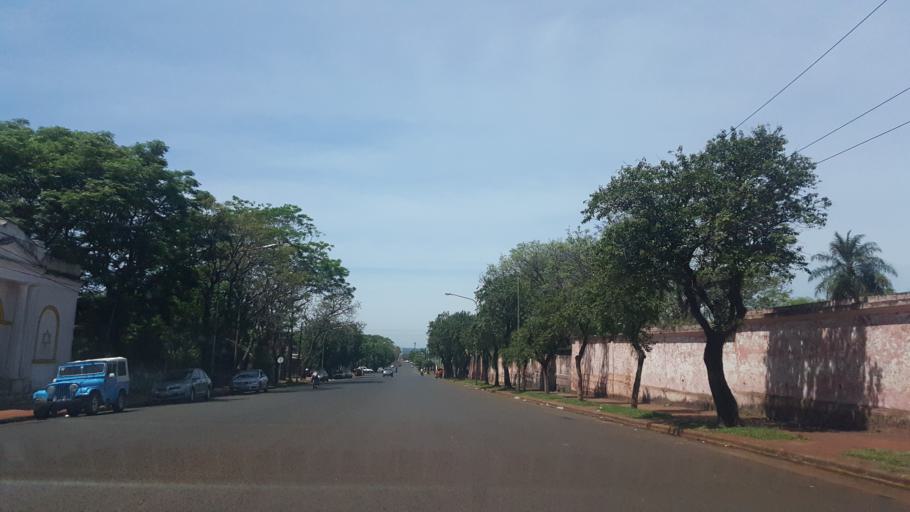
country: AR
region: Misiones
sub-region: Departamento de Capital
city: Posadas
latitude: -27.3796
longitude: -55.9124
